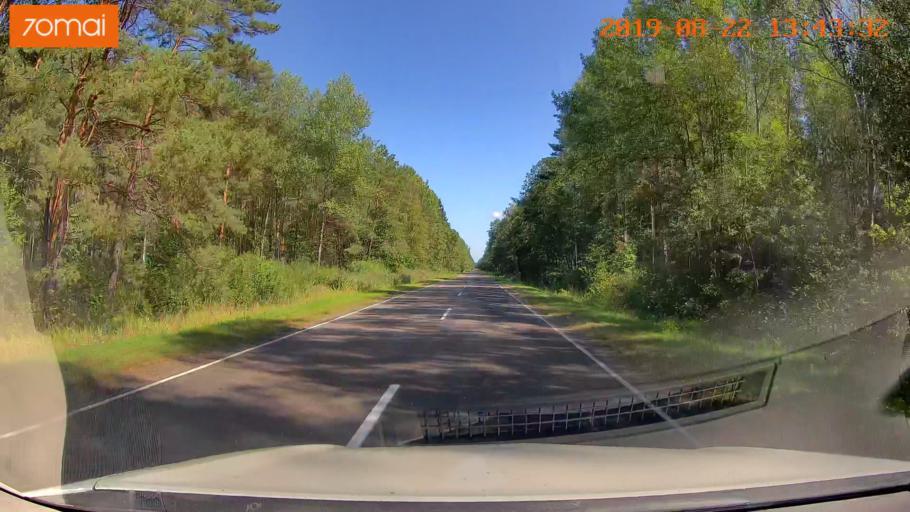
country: BY
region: Mogilev
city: Asipovichy
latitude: 53.2429
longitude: 28.4400
